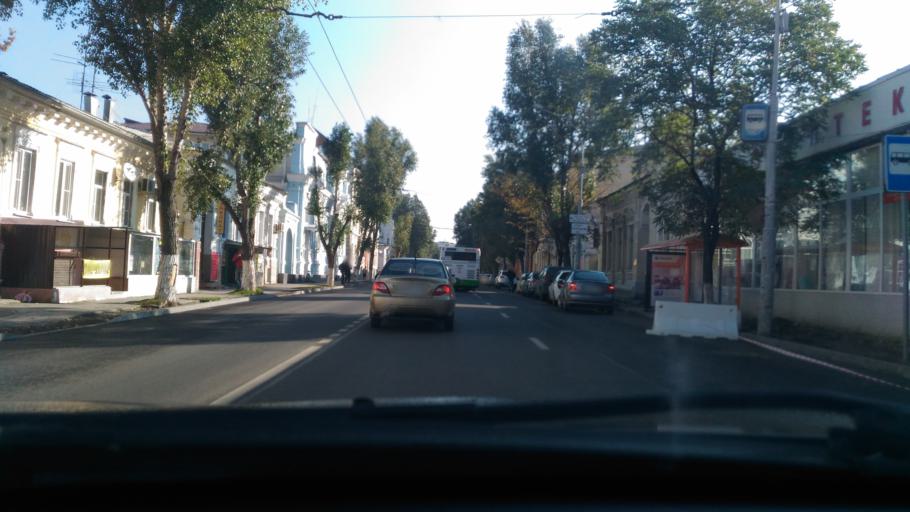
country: RU
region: Rostov
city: Rostov-na-Donu
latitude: 47.2295
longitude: 39.7577
